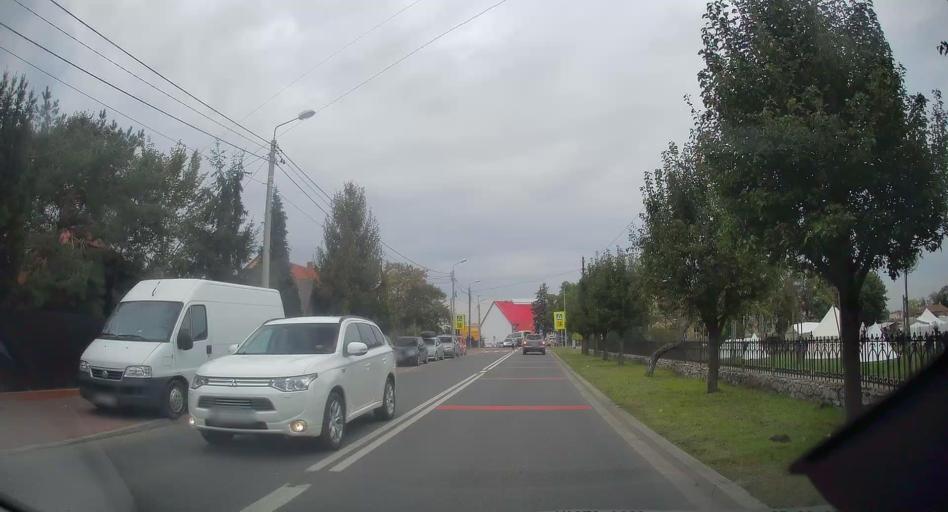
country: PL
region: Lesser Poland Voivodeship
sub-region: Powiat wielicki
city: Niepolomice
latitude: 50.0345
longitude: 20.2157
